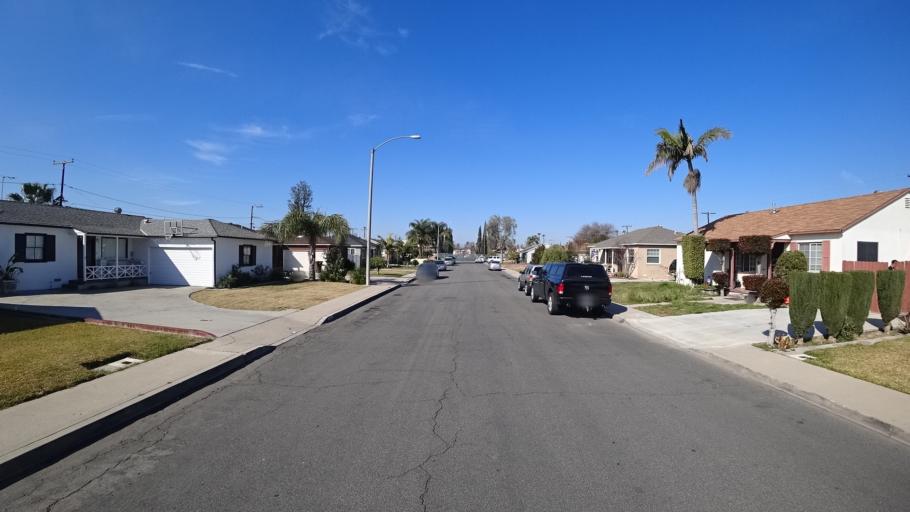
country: US
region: California
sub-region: Orange County
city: Anaheim
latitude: 33.8487
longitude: -117.9262
